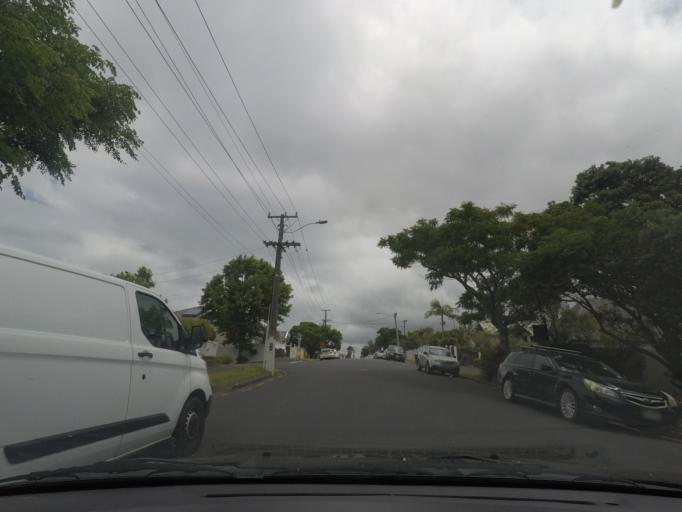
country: NZ
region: Auckland
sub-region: Auckland
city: Auckland
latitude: -36.8662
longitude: 174.7846
